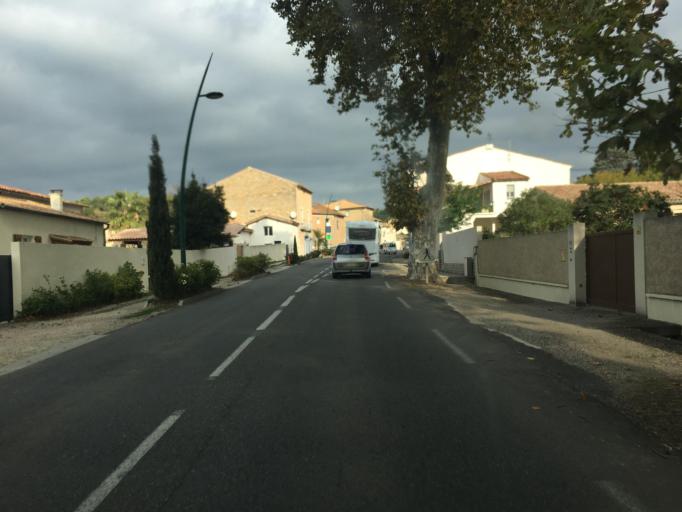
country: FR
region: Languedoc-Roussillon
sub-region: Departement de l'Herault
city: Nebian
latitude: 43.6051
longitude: 3.4367
